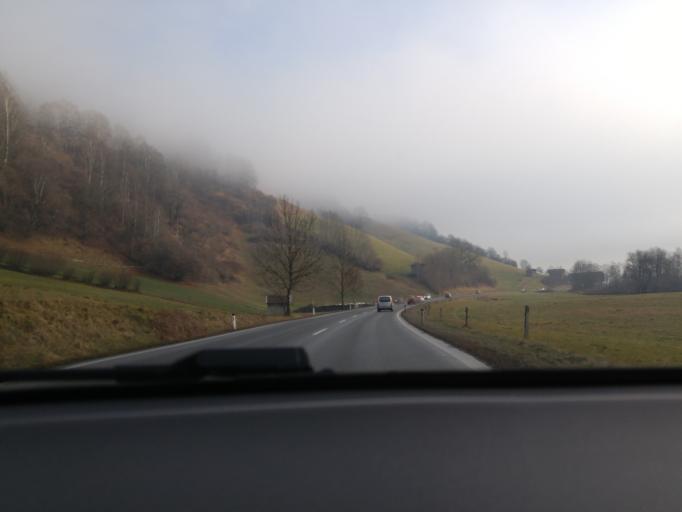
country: AT
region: Salzburg
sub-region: Politischer Bezirk Zell am See
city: Niedernsill
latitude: 47.2860
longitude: 12.6510
